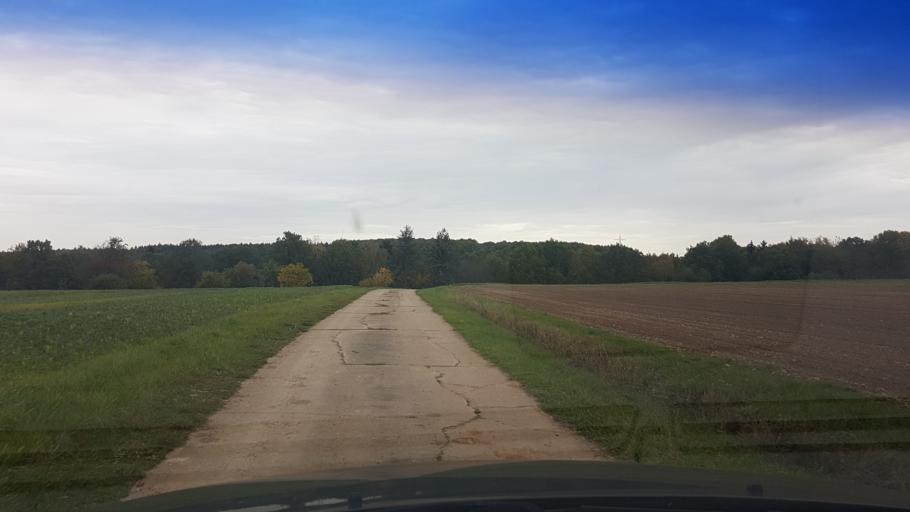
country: DE
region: Bavaria
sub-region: Upper Franconia
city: Zapfendorf
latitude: 49.9796
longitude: 10.9341
